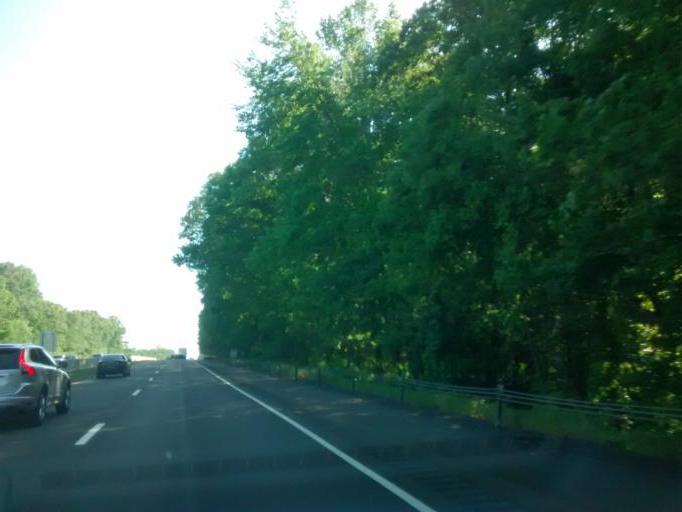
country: US
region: Connecticut
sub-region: New London County
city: Niantic
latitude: 41.3504
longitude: -72.2222
